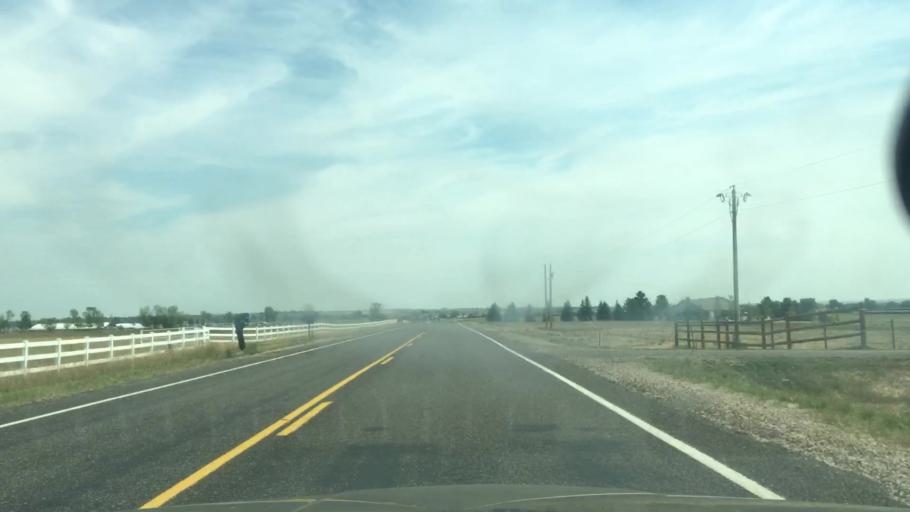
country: US
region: Colorado
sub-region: Larimer County
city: Berthoud
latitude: 40.3345
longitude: -105.1622
